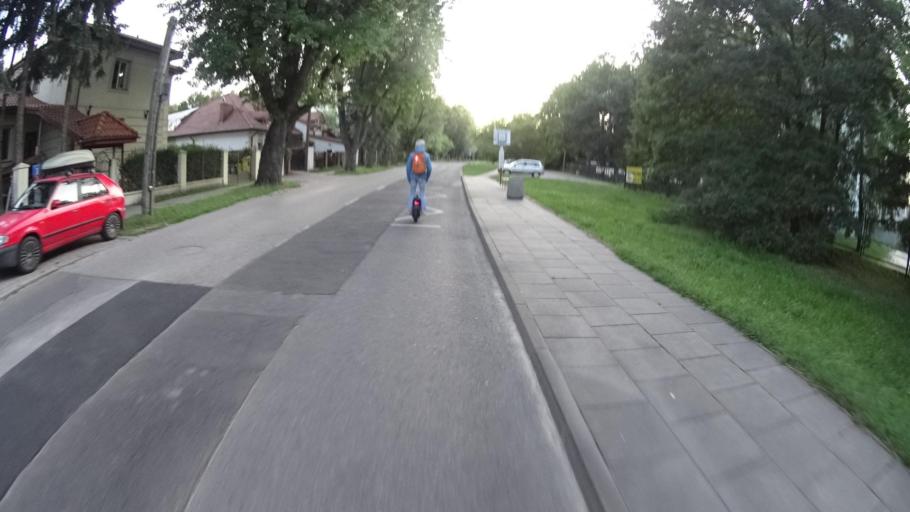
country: PL
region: Masovian Voivodeship
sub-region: Warszawa
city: Bielany
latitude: 52.3088
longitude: 20.9258
